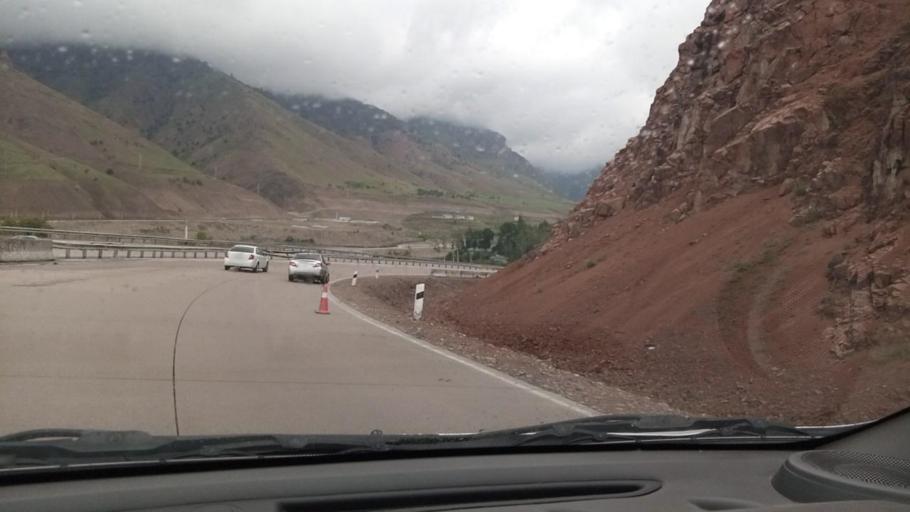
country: UZ
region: Toshkent
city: Angren
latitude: 41.1528
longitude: 70.4446
